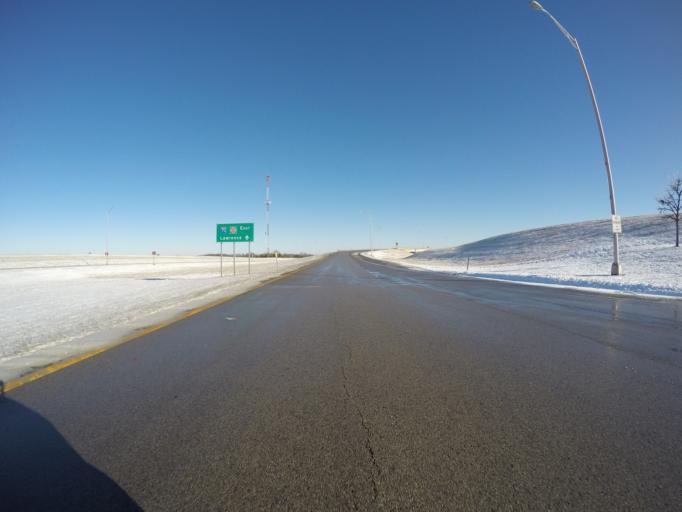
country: US
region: Kansas
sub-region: Shawnee County
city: Topeka
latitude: 39.0192
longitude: -95.5067
